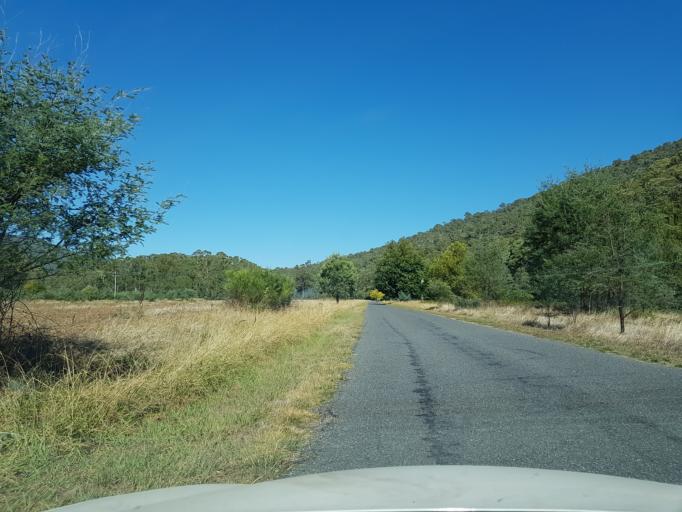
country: AU
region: Victoria
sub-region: Mansfield
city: Mansfield
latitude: -36.8699
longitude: 146.3772
